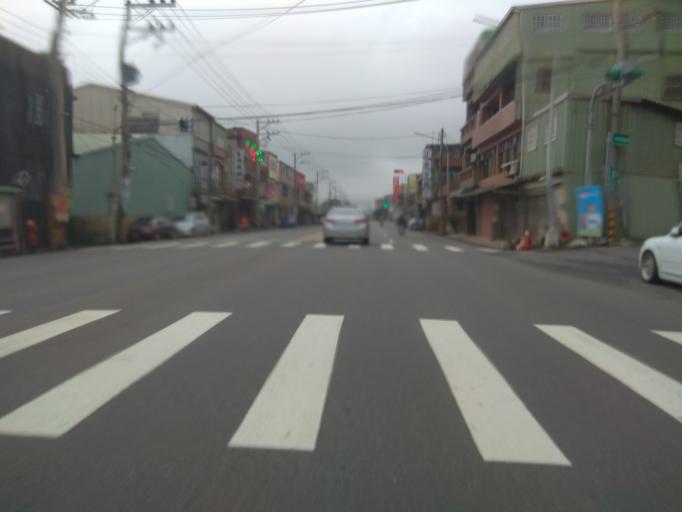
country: TW
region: Taiwan
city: Taoyuan City
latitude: 25.0297
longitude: 121.1058
